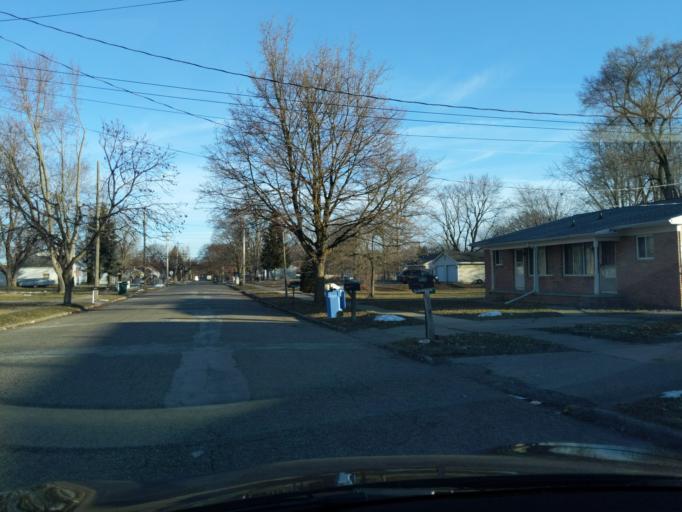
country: US
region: Michigan
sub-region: Ingham County
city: Lansing
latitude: 42.6919
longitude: -84.5631
